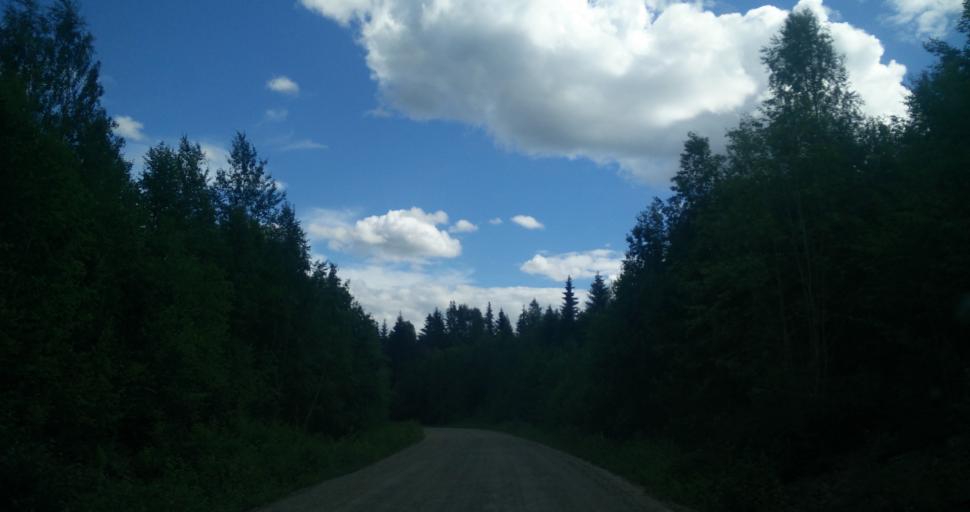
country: SE
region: Gaevleborg
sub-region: Nordanstigs Kommun
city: Bergsjoe
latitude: 62.0584
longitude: 16.7827
